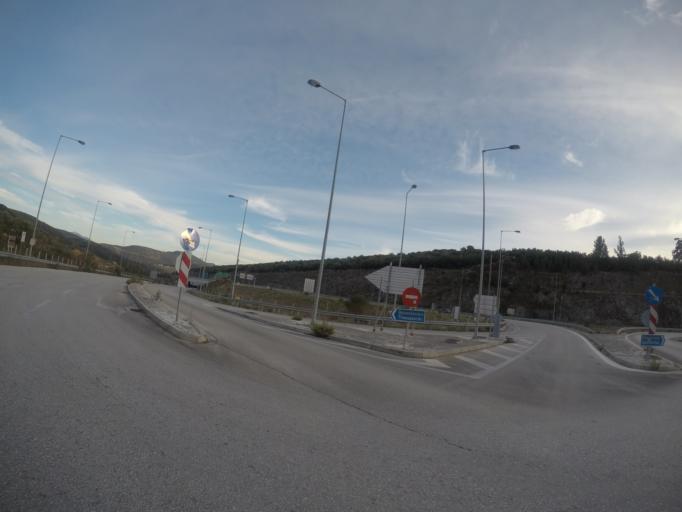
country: GR
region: Epirus
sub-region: Nomos Thesprotias
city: Plataria
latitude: 39.4515
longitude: 20.3593
